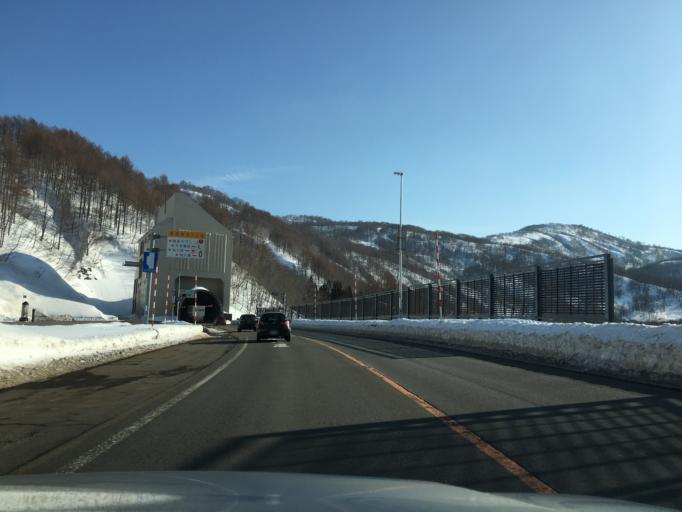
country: JP
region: Yamagata
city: Tsuruoka
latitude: 38.5251
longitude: 139.9492
